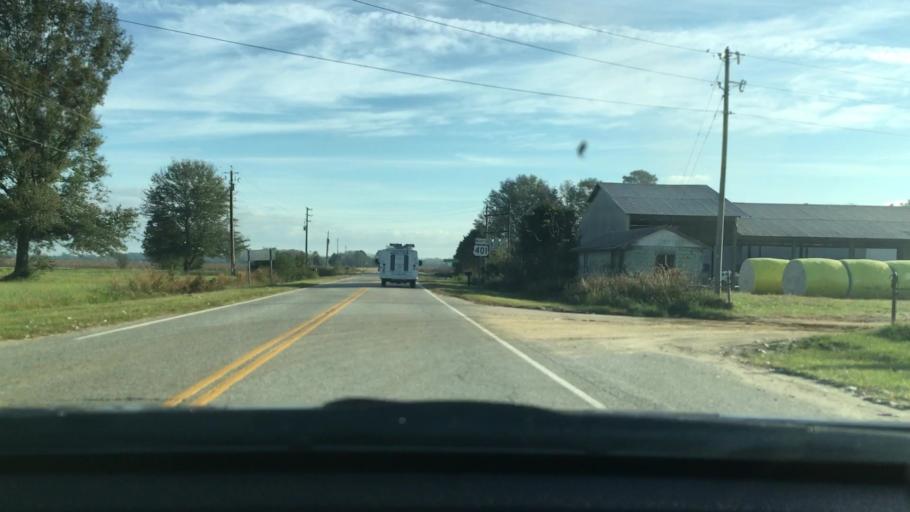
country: US
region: South Carolina
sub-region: Lee County
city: Bishopville
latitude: 34.0664
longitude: -80.2181
